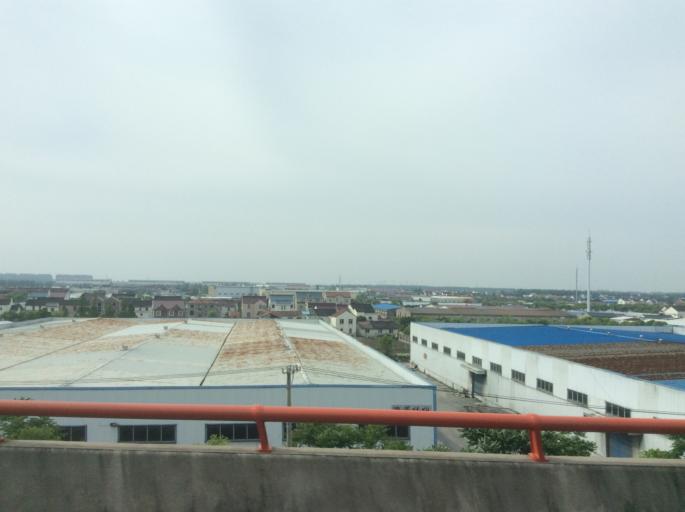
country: CN
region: Shanghai Shi
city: Kangqiao
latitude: 31.2087
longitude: 121.7345
